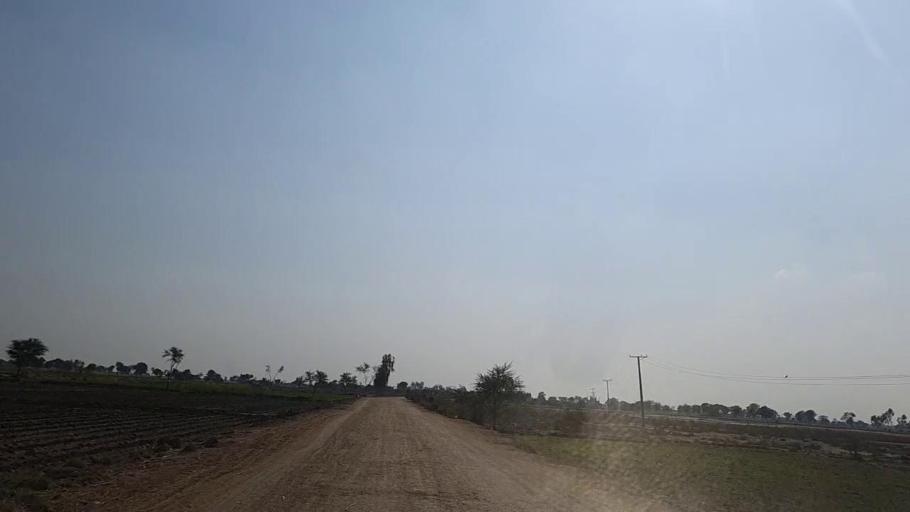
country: PK
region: Sindh
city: Daur
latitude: 26.4565
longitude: 68.2502
